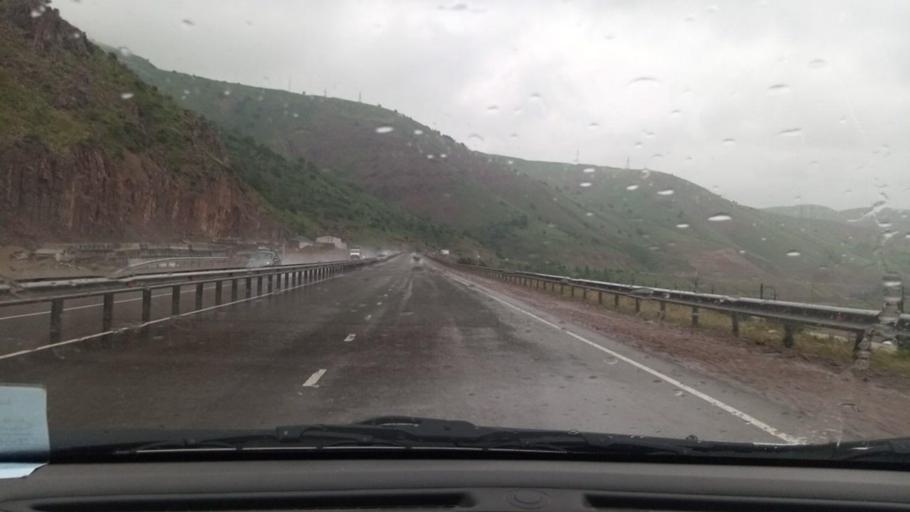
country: UZ
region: Toshkent
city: Angren
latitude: 41.0872
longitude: 70.3227
